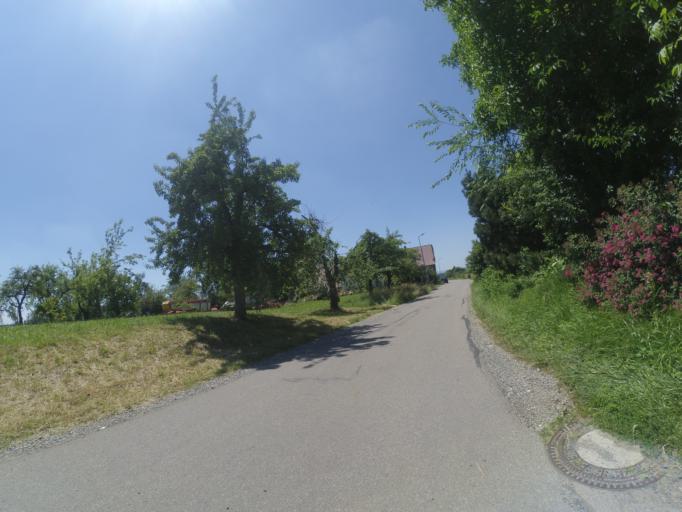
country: DE
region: Baden-Wuerttemberg
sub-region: Tuebingen Region
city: Bad Waldsee
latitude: 47.9010
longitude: 9.8086
